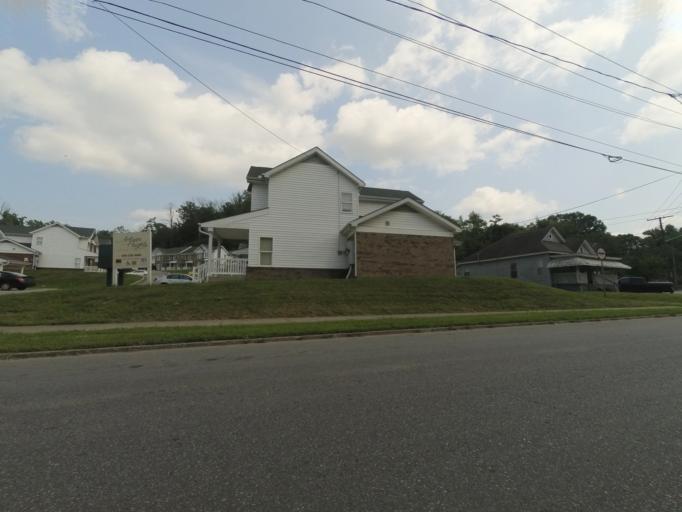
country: US
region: West Virginia
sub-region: Cabell County
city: Huntington
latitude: 38.4195
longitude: -82.4089
